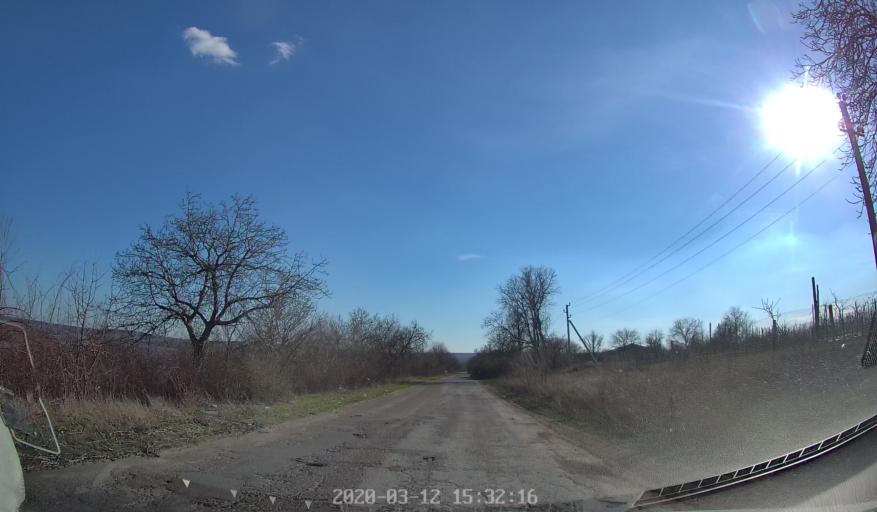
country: MD
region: Chisinau
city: Ciorescu
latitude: 47.1532
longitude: 28.9413
